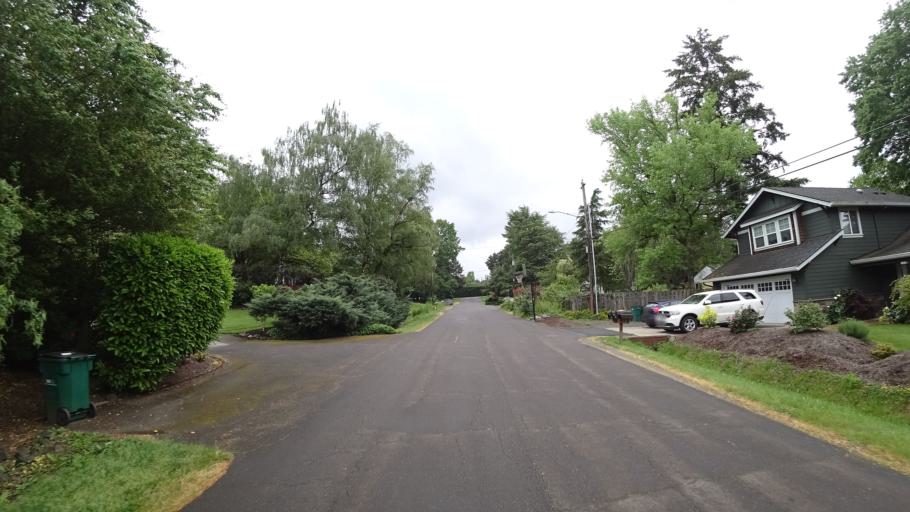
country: US
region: Oregon
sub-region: Washington County
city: Garden Home-Whitford
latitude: 45.4673
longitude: -122.7687
